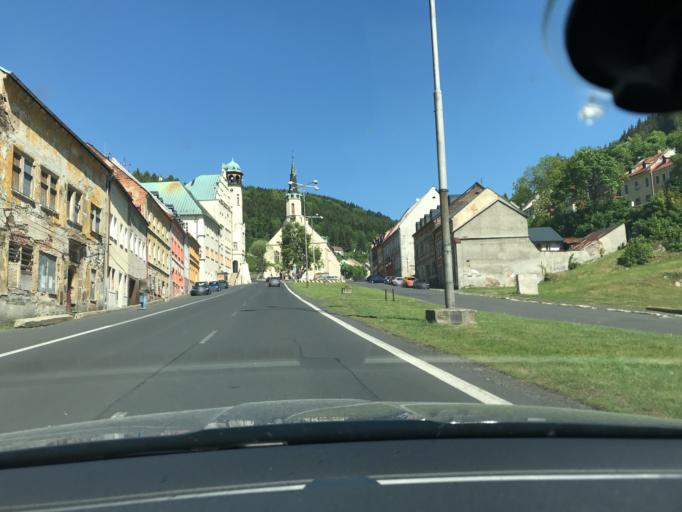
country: CZ
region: Karlovarsky
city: Jachymov
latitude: 50.3704
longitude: 12.9152
